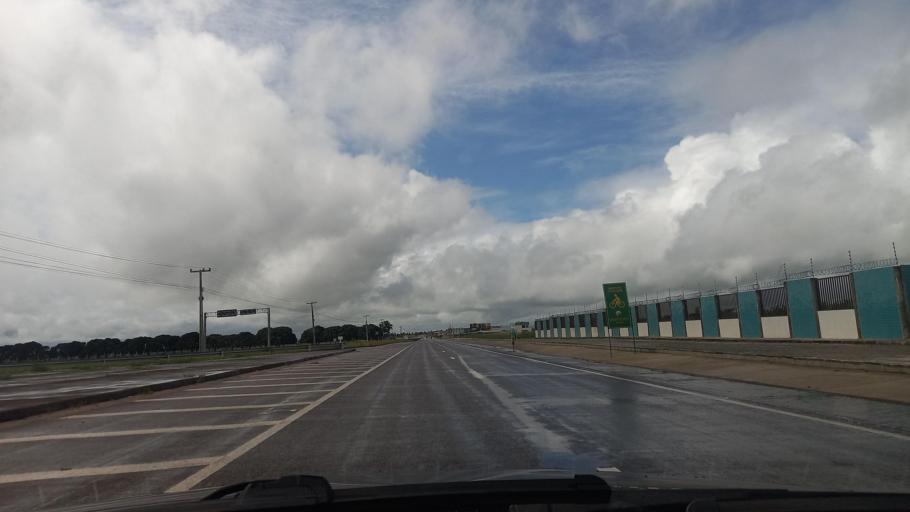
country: BR
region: Alagoas
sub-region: Limoeiro De Anadia
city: Limoeiro de Anadia
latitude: -9.7582
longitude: -36.5523
